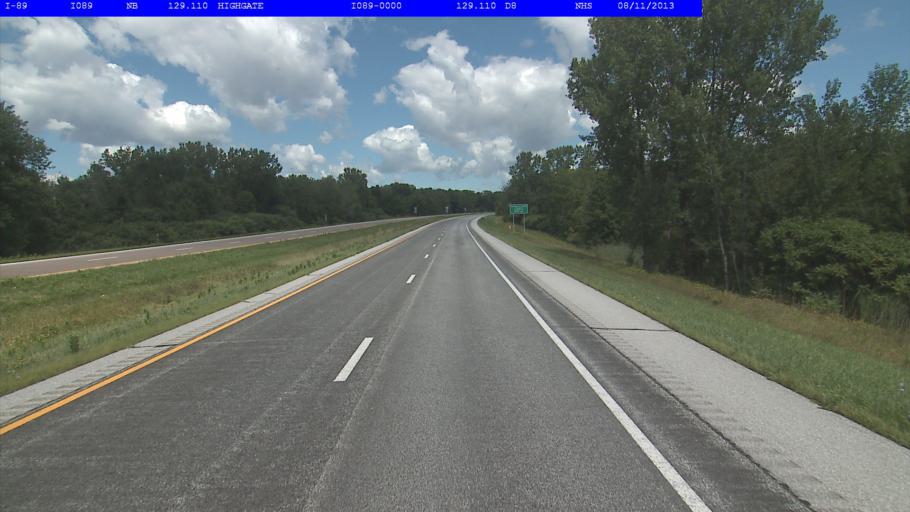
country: US
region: Vermont
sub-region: Franklin County
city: Swanton
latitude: 44.9991
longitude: -73.0864
